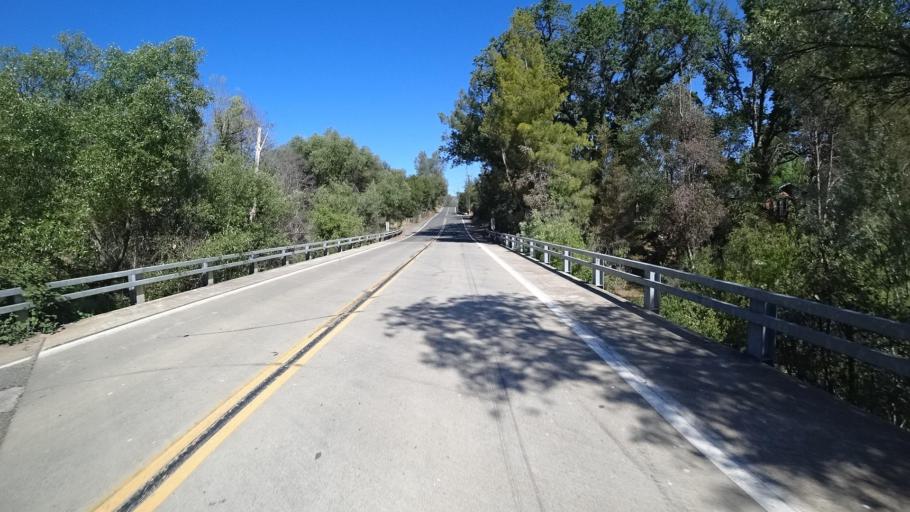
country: US
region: California
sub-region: Lake County
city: Clearlake Oaks
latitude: 39.0482
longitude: -122.5799
